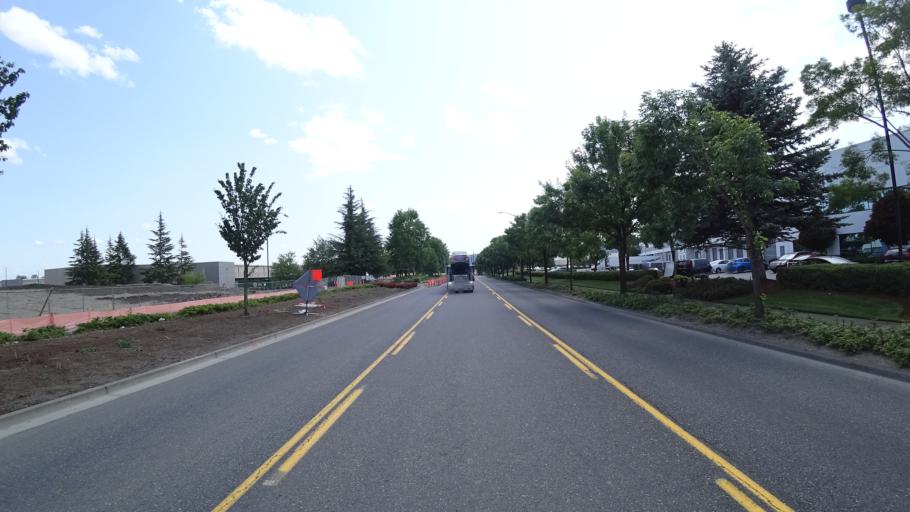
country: US
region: Washington
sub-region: Clark County
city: Lake Shore
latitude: 45.6322
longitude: -122.7720
